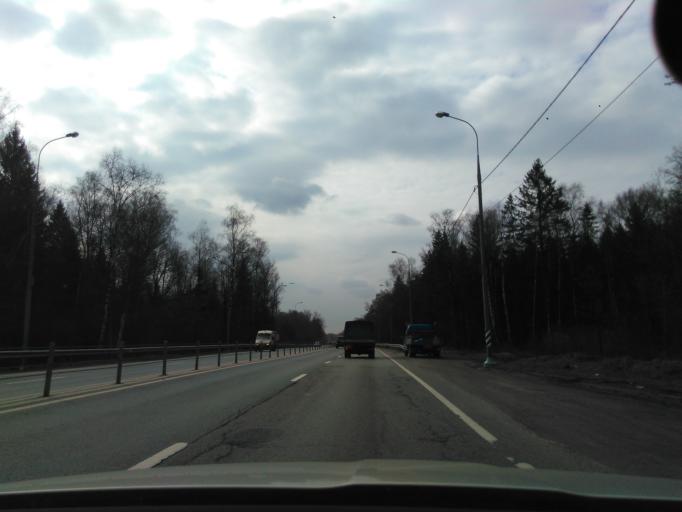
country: RU
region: Moskovskaya
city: Marfino
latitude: 56.0287
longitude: 37.5426
